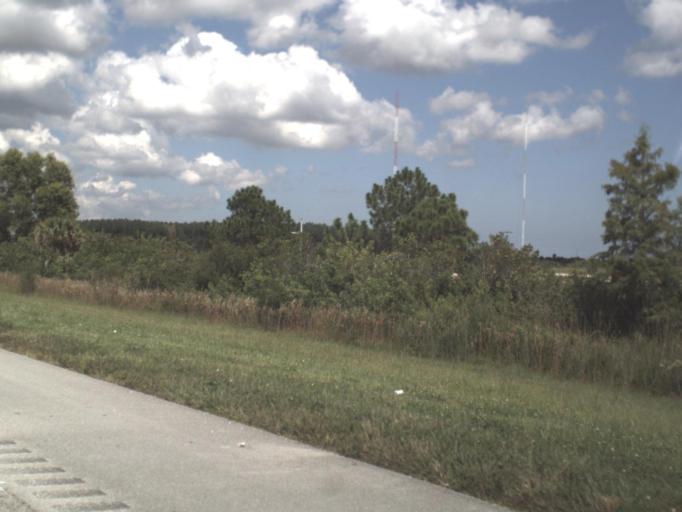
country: US
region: Florida
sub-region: Palm Beach County
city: Tequesta
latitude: 26.9918
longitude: -80.1931
